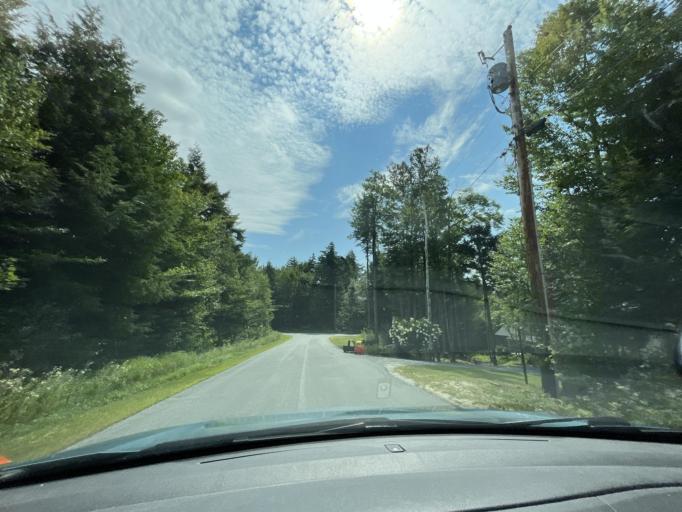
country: US
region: New Hampshire
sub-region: Merrimack County
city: New London
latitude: 43.4054
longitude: -71.9990
